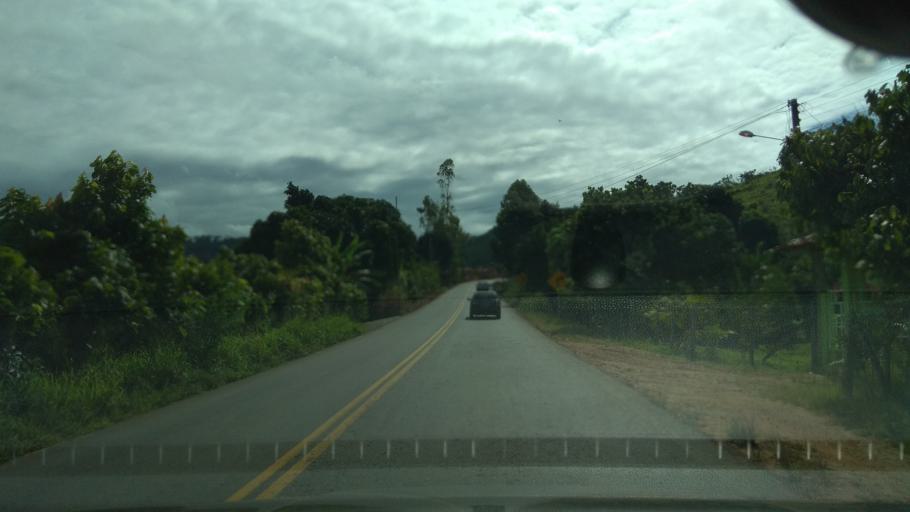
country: BR
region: Bahia
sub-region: Ubaira
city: Ubaira
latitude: -13.2702
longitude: -39.6303
